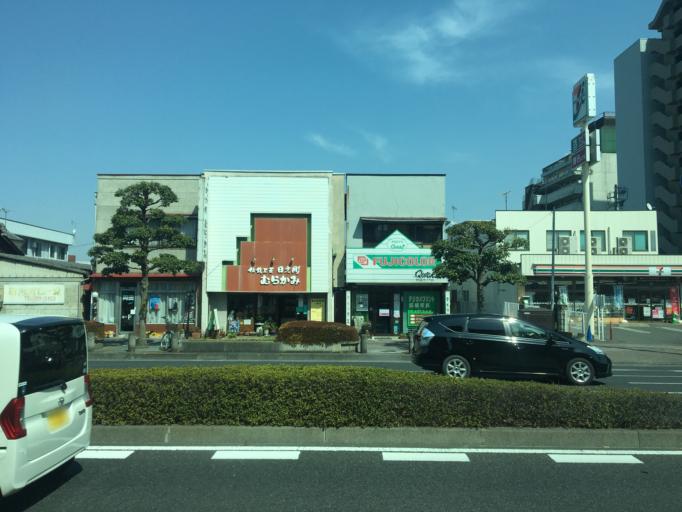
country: JP
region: Tochigi
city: Utsunomiya-shi
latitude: 36.5625
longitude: 139.8726
